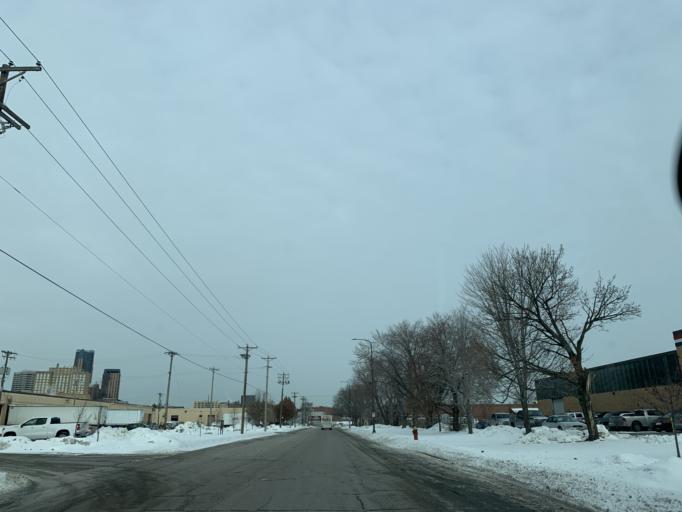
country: US
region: Minnesota
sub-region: Ramsey County
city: Saint Paul
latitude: 44.9411
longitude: -93.0789
